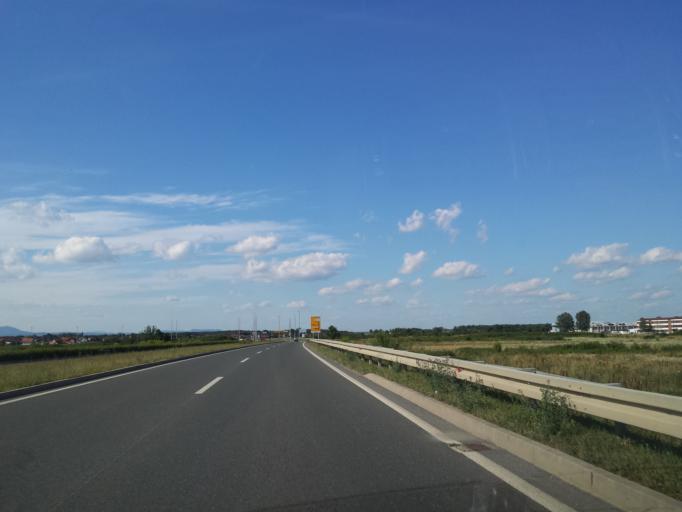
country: HR
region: Zagrebacka
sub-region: Grad Velika Gorica
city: Velika Gorica
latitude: 45.7147
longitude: 16.0857
